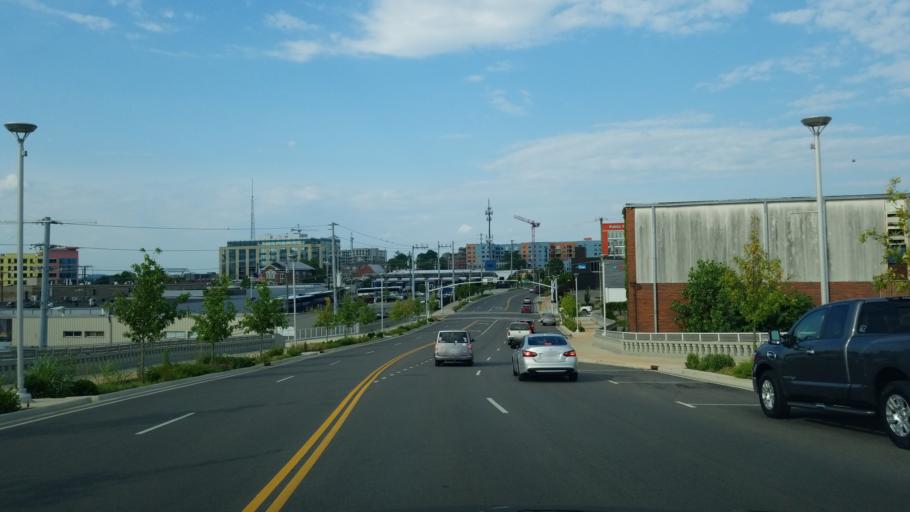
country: US
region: Tennessee
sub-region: Davidson County
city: Nashville
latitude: 36.1504
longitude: -86.7753
